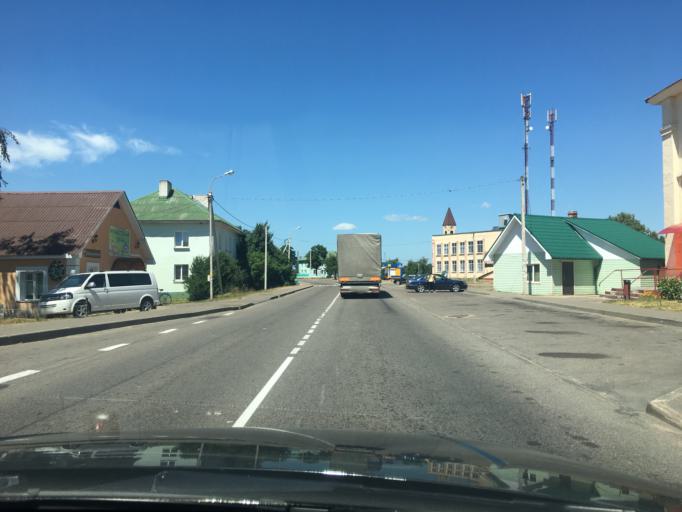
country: BY
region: Grodnenskaya
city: Iwye
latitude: 54.0316
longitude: 25.9272
